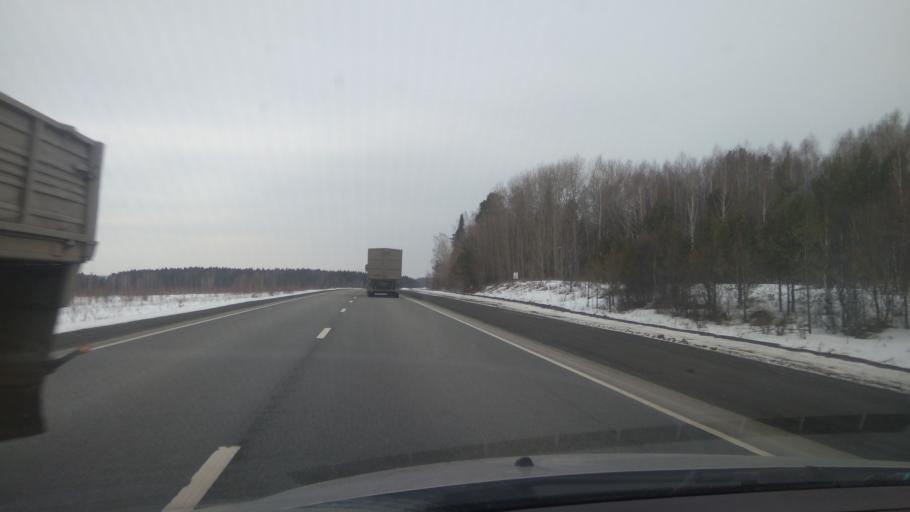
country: RU
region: Sverdlovsk
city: Bisert'
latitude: 56.8144
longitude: 58.7449
